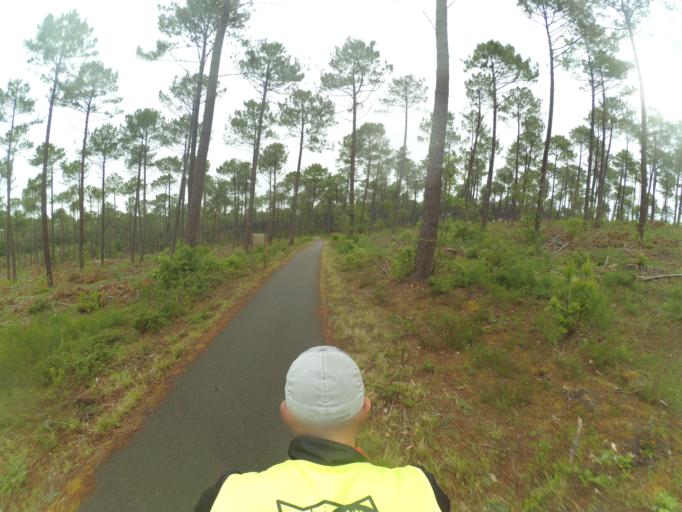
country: FR
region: Aquitaine
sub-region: Departement des Landes
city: Mimizan
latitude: 44.2194
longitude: -1.2509
